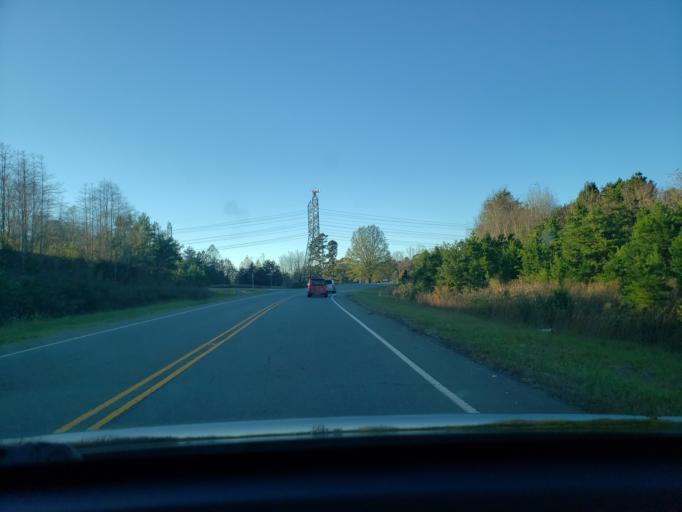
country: US
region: North Carolina
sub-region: Forsyth County
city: Walkertown
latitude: 36.1947
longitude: -80.1627
